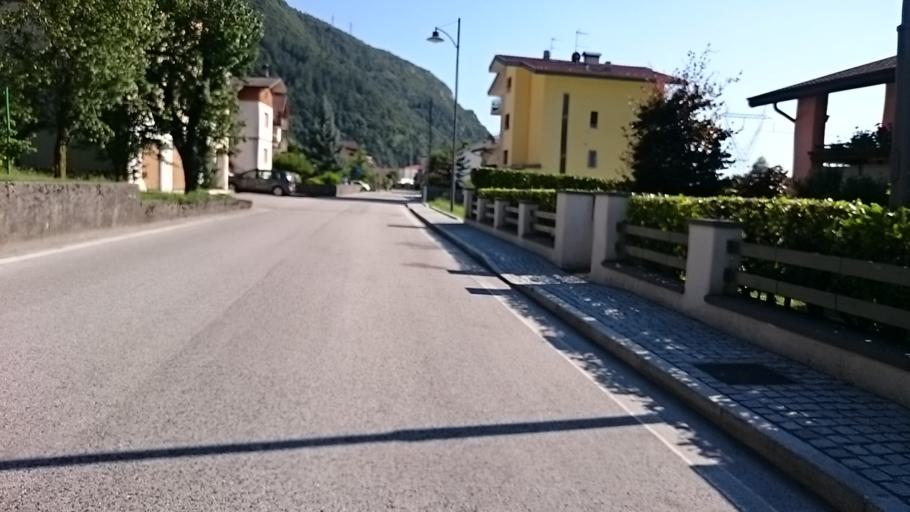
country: IT
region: Veneto
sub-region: Provincia di Belluno
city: Soverzene
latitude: 46.2062
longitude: 12.3029
